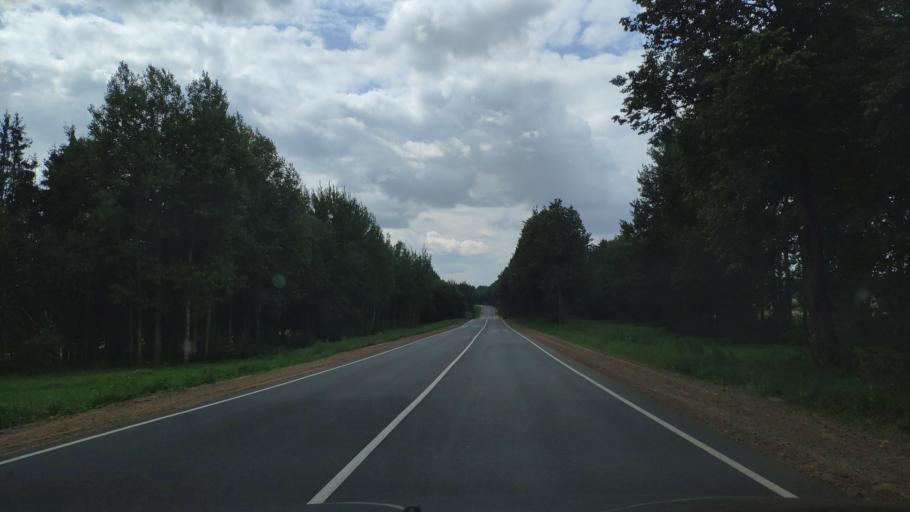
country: BY
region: Minsk
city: Syomkava
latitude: 54.0085
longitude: 27.3903
